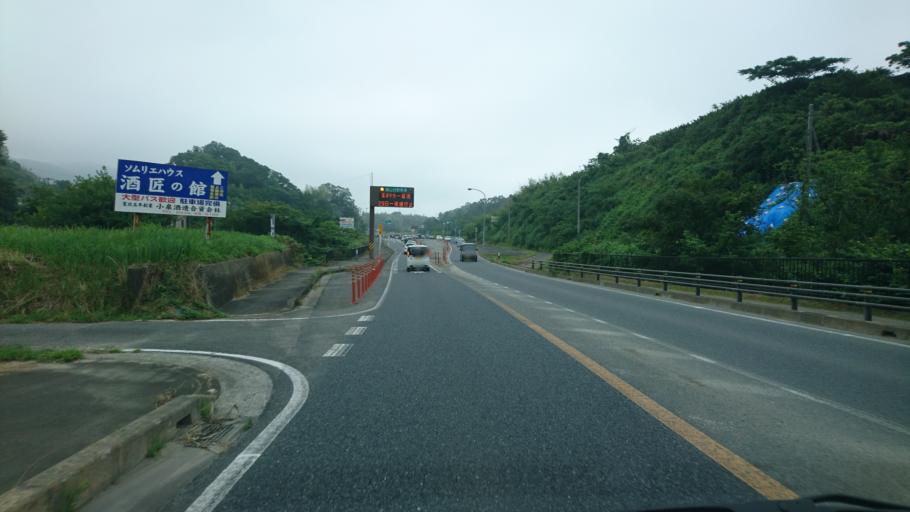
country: JP
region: Chiba
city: Kimitsu
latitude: 35.2523
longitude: 139.8848
